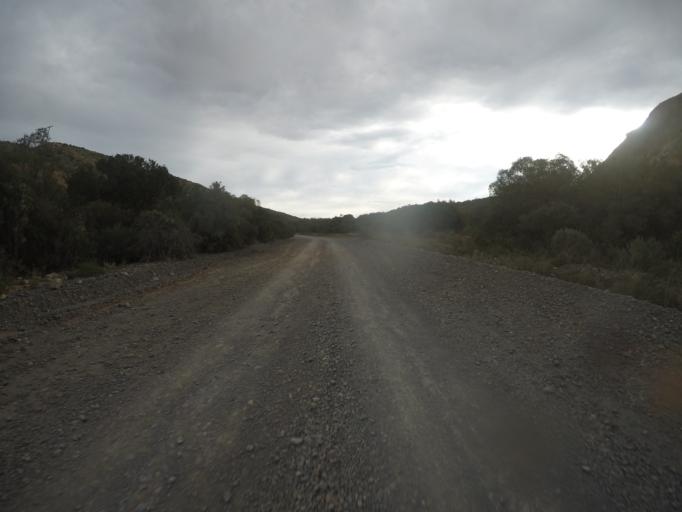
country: ZA
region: Eastern Cape
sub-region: Cacadu District Municipality
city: Willowmore
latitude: -33.5139
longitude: 23.8172
